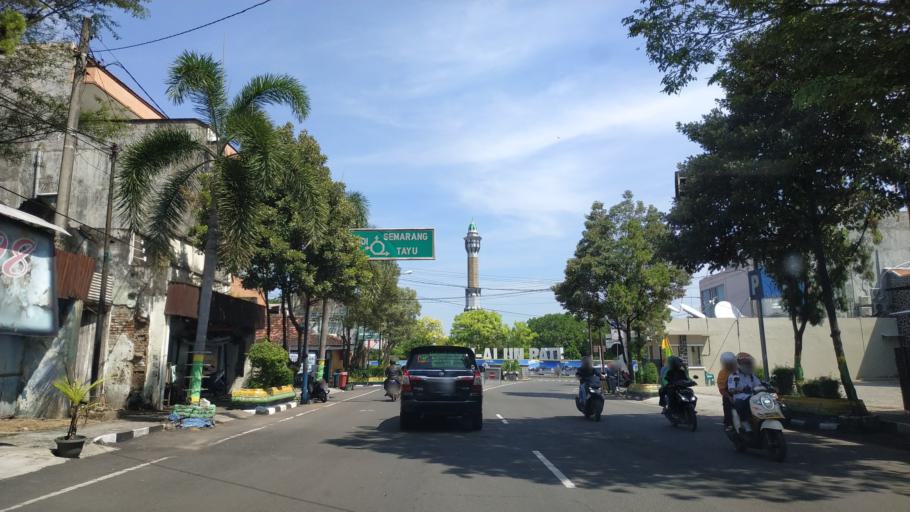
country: ID
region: Central Java
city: Pati
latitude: -6.7537
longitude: 111.0411
